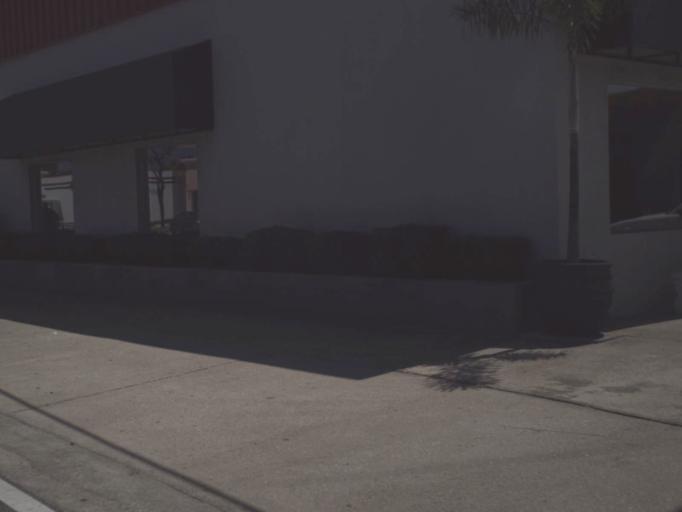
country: US
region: Florida
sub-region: Brevard County
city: Melbourne
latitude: 28.0672
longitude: -80.5994
